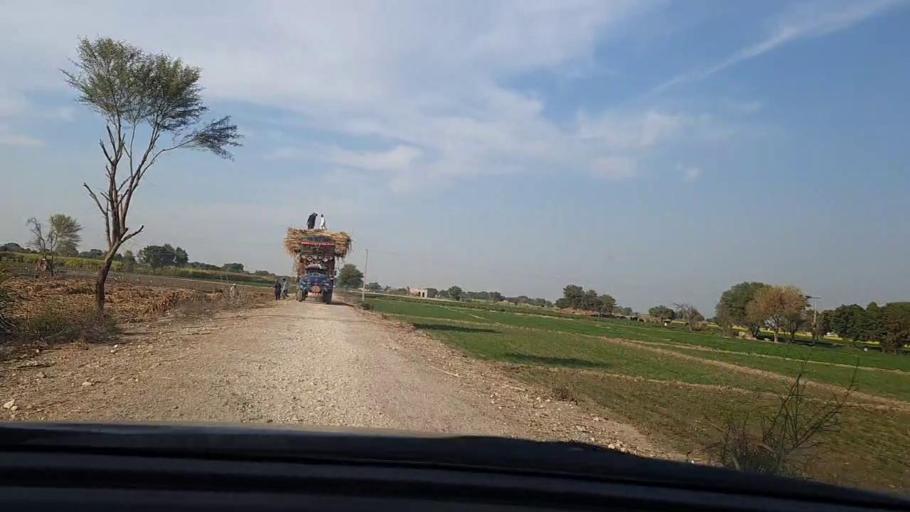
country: PK
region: Sindh
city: Daulatpur
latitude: 26.3254
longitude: 68.0266
